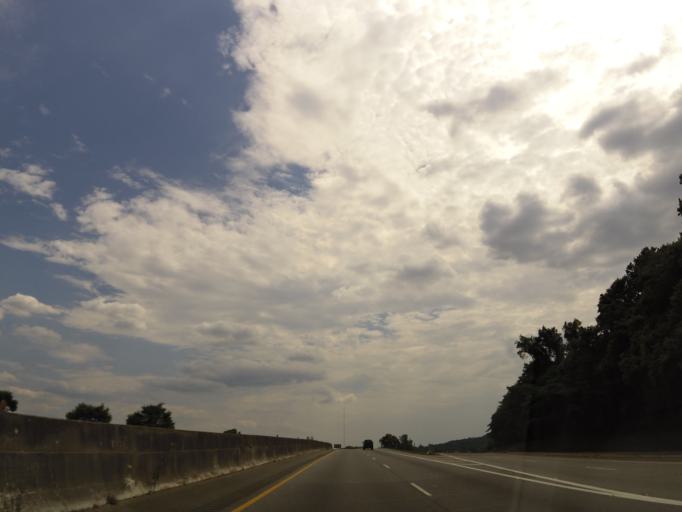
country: US
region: Tennessee
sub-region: Marion County
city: South Pittsburg
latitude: 35.0212
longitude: -85.6964
